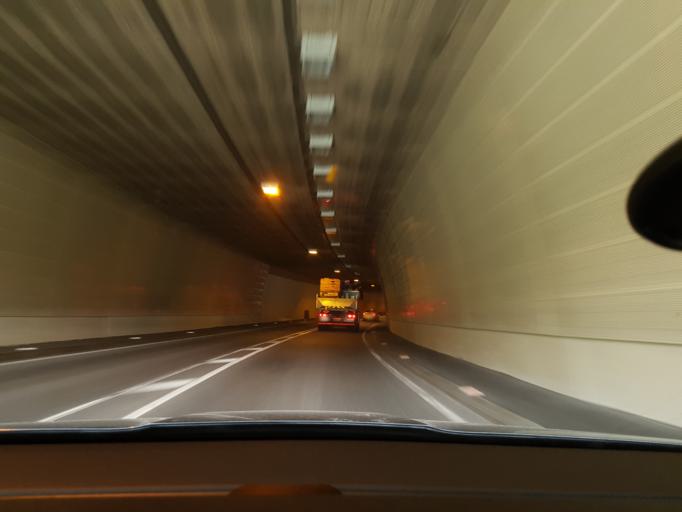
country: AT
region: Salzburg
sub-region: Politischer Bezirk Zell am See
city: Wald im Pinzgau
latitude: 47.2449
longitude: 12.2276
